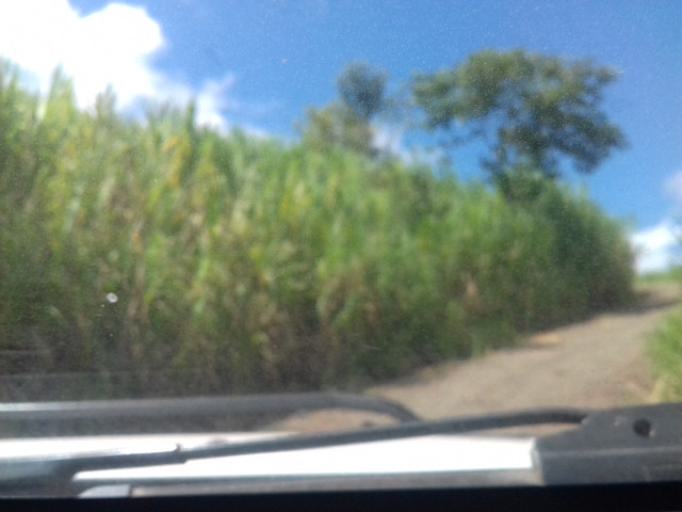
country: NI
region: Atlantico Norte (RAAN)
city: Waslala
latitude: 13.2266
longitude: -85.5716
